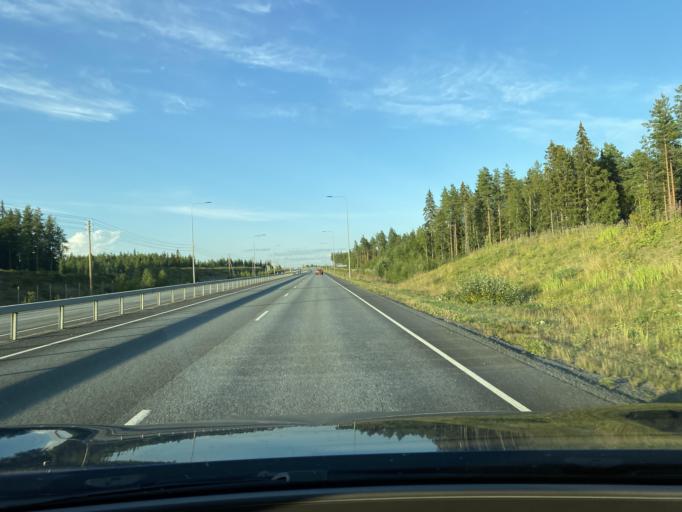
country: FI
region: Southern Ostrobothnia
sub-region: Seinaejoki
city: Nurmo
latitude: 62.7343
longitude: 22.9020
